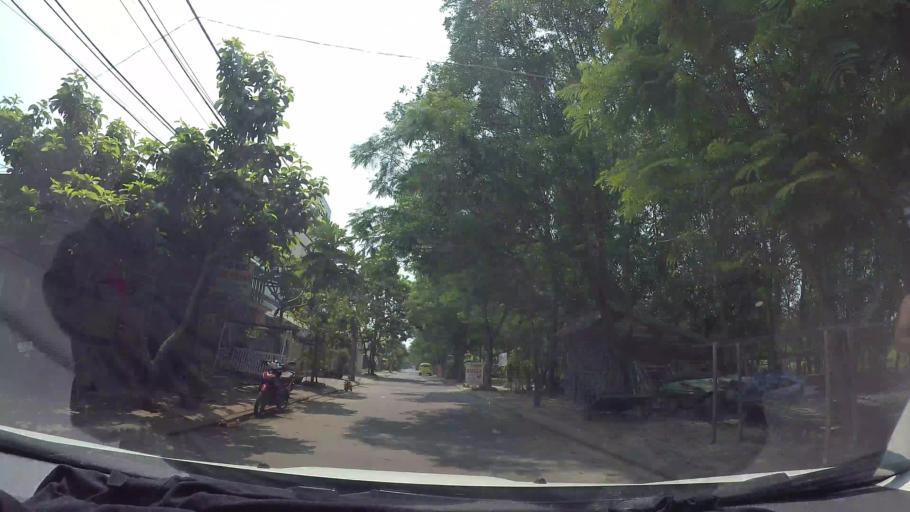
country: VN
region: Da Nang
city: Cam Le
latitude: 15.9891
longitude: 108.2066
